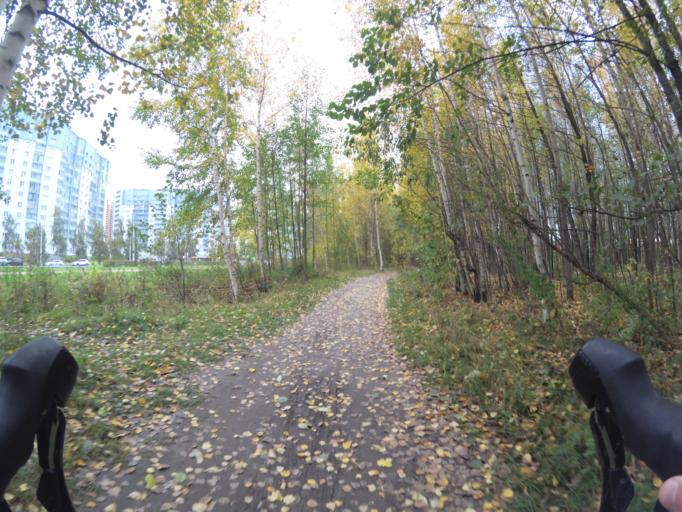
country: RU
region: Leningrad
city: Untolovo
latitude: 59.9974
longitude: 30.1920
